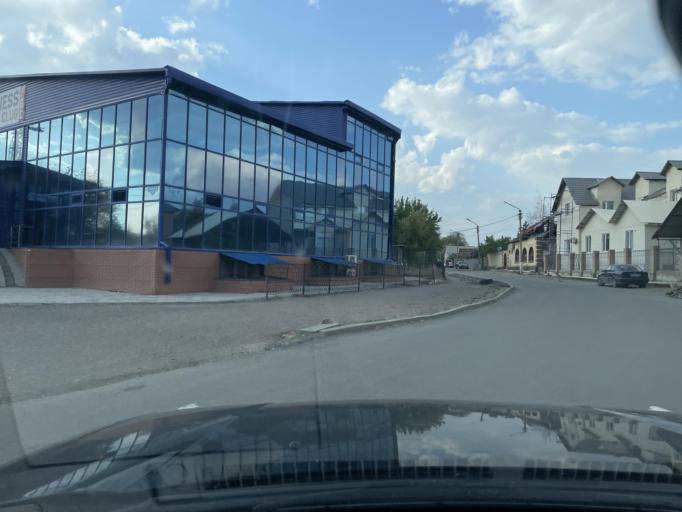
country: KZ
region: Qaraghandy
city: Zhezqazghan
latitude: 47.7923
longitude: 67.7096
